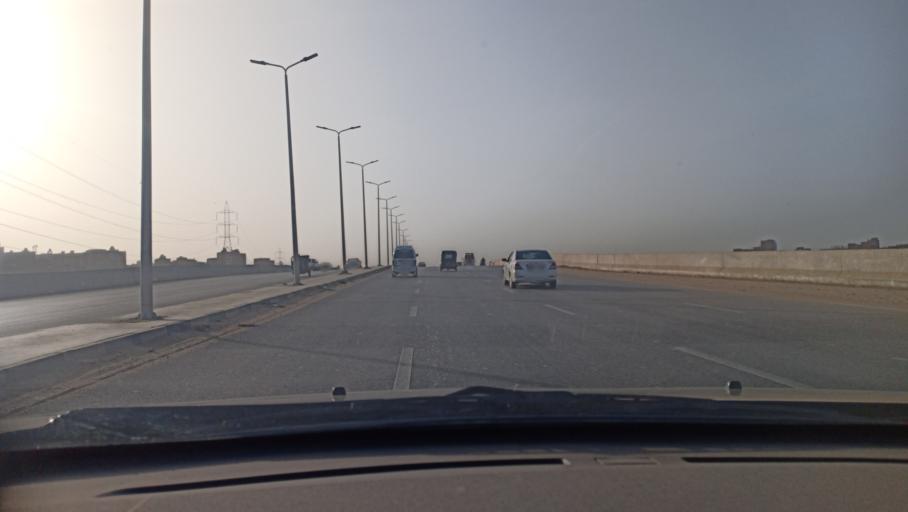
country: EG
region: Muhafazat al Qalyubiyah
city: Qalyub
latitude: 30.1423
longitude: 31.2630
